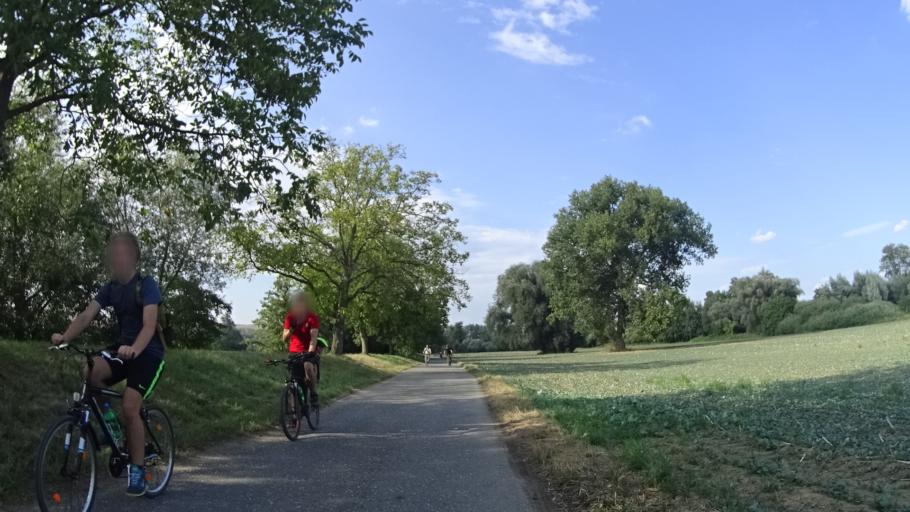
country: CZ
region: Zlin
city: Spytihnev
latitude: 49.1415
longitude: 17.5055
